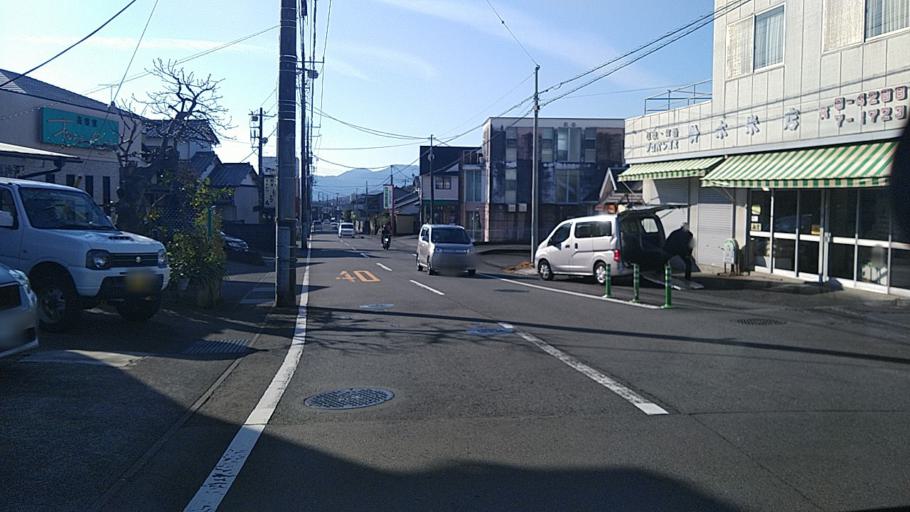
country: JP
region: Shizuoka
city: Fujinomiya
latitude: 35.2345
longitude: 138.6172
